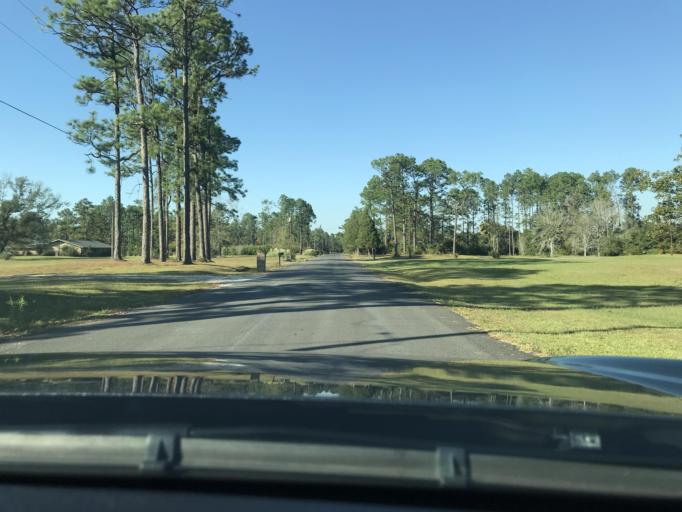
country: US
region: Louisiana
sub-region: Calcasieu Parish
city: Westlake
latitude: 30.3171
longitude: -93.2688
